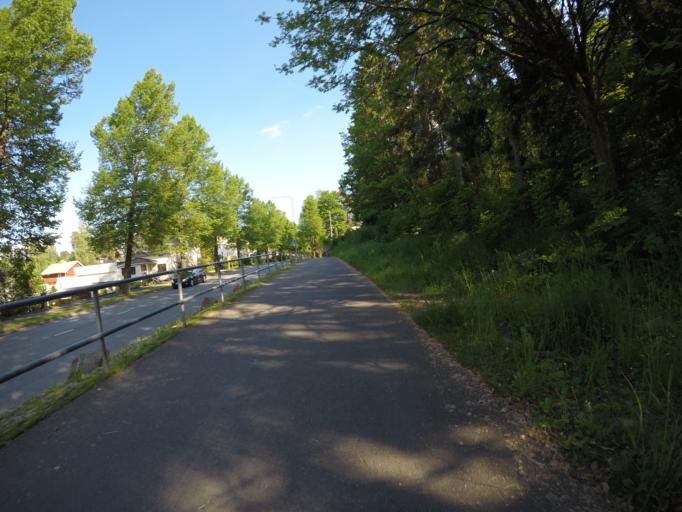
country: FI
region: Haeme
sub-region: Haemeenlinna
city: Haemeenlinna
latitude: 61.0098
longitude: 24.4671
